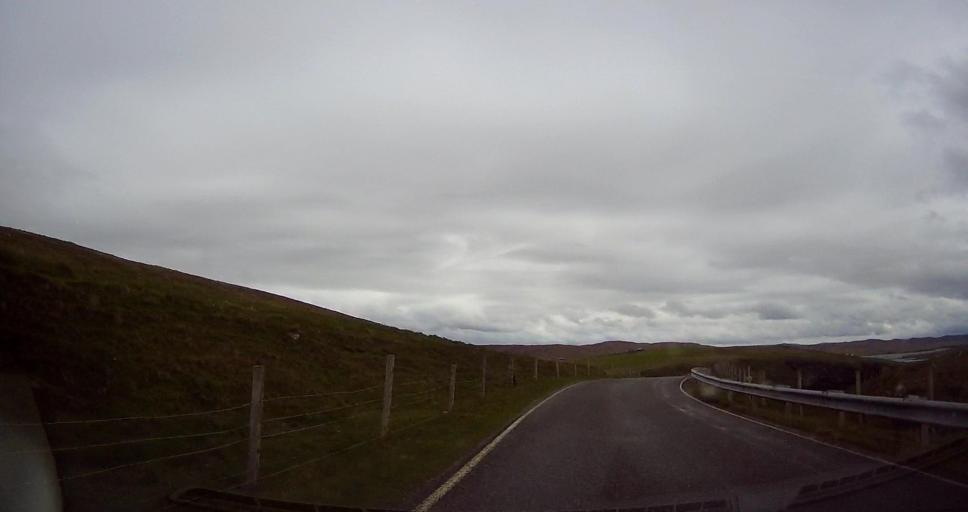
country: GB
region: Scotland
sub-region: Shetland Islands
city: Lerwick
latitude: 60.4857
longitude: -1.5063
